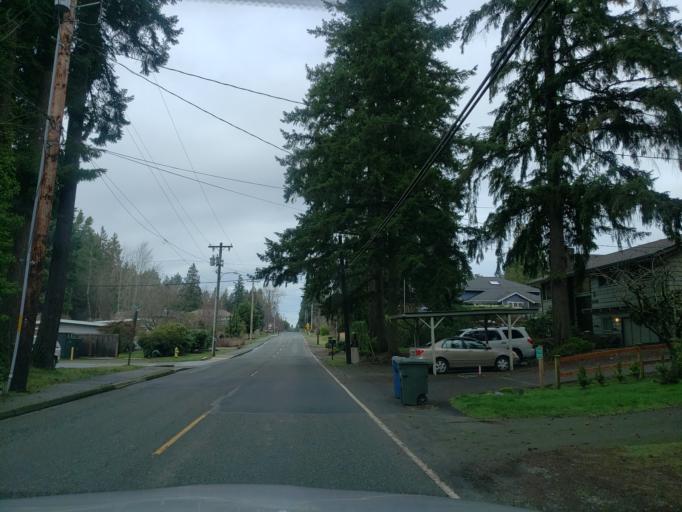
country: US
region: Washington
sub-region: Snohomish County
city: Lynnwood
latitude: 47.8233
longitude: -122.3414
